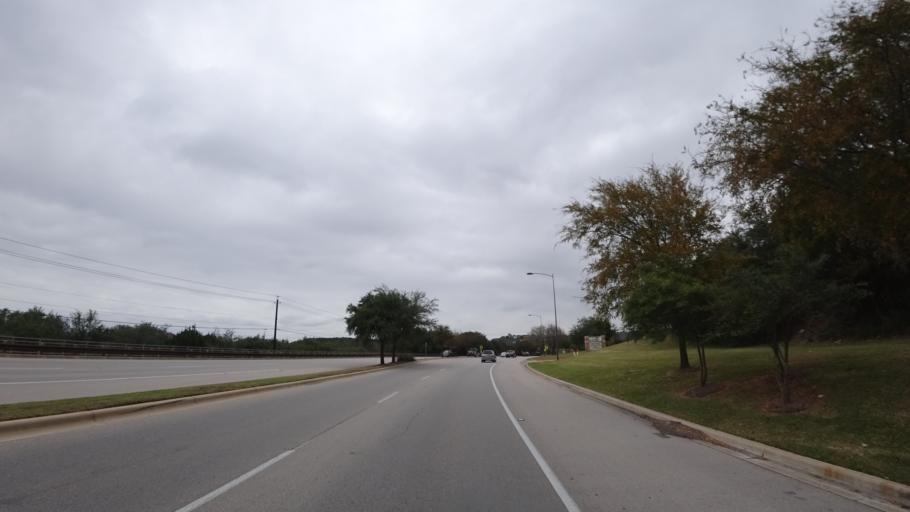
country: US
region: Texas
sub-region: Travis County
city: Hudson Bend
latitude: 30.3795
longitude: -97.8850
